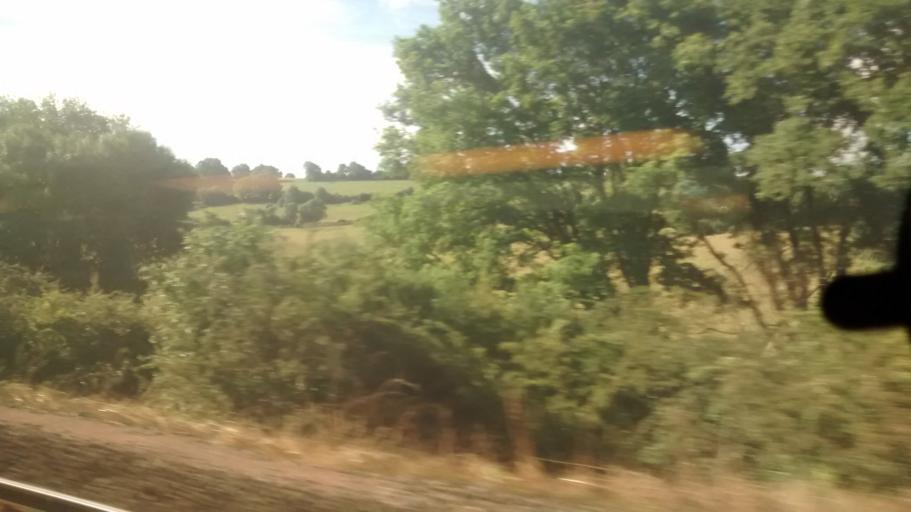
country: FR
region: Pays de la Loire
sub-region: Departement de la Mayenne
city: Sainte-Suzanne
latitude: 48.1354
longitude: -0.3022
